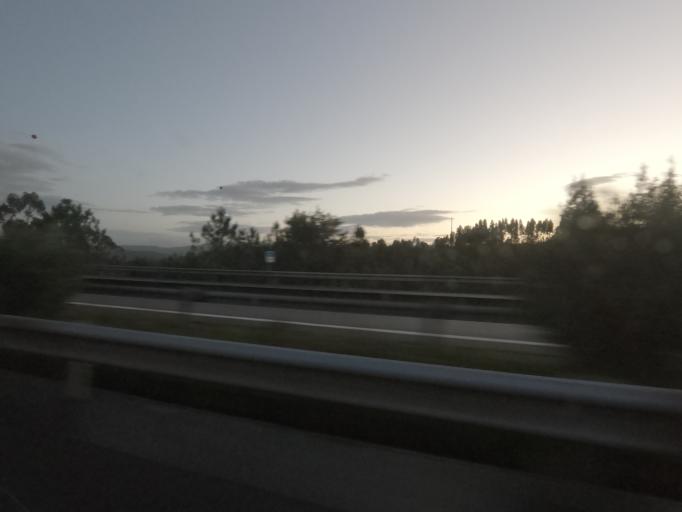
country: PT
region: Porto
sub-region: Paredes
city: Recarei
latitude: 41.1740
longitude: -8.4149
